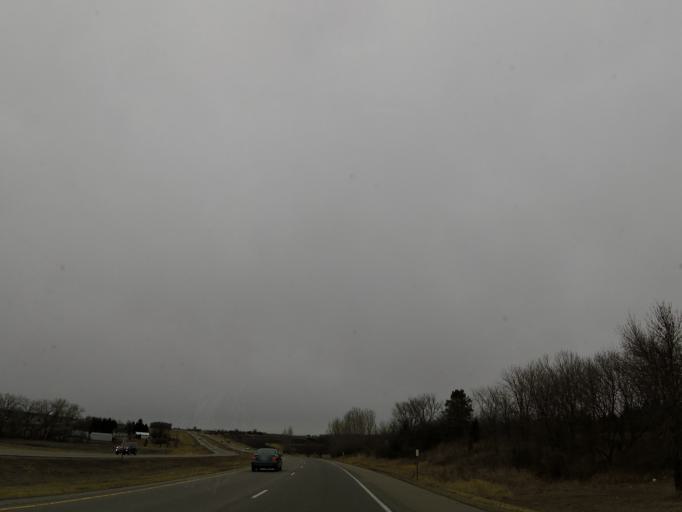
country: US
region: Minnesota
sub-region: Le Sueur County
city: Le Sueur
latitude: 44.5188
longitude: -93.8468
